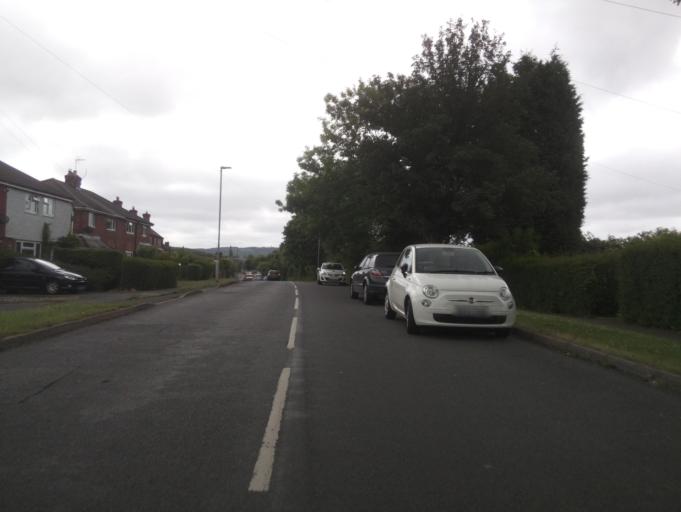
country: GB
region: England
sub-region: Leicestershire
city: Coalville
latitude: 52.7353
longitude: -1.3527
